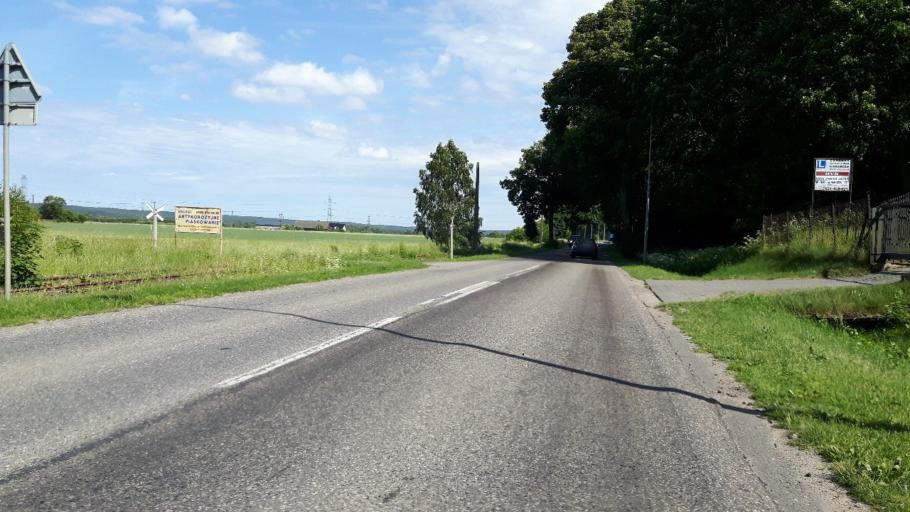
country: PL
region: Pomeranian Voivodeship
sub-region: Powiat wejherowski
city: Orle
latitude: 54.6475
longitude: 18.1096
